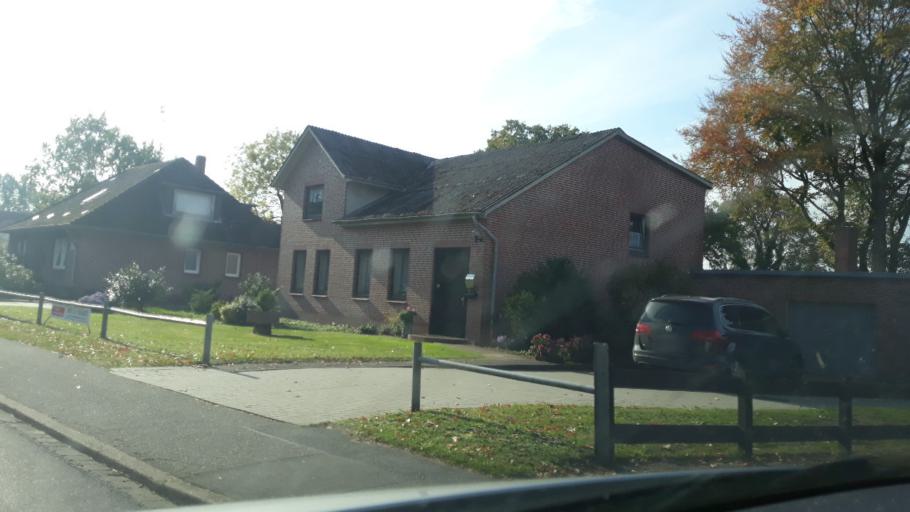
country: DE
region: Schleswig-Holstein
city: Kropp
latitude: 54.4083
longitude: 9.5096
